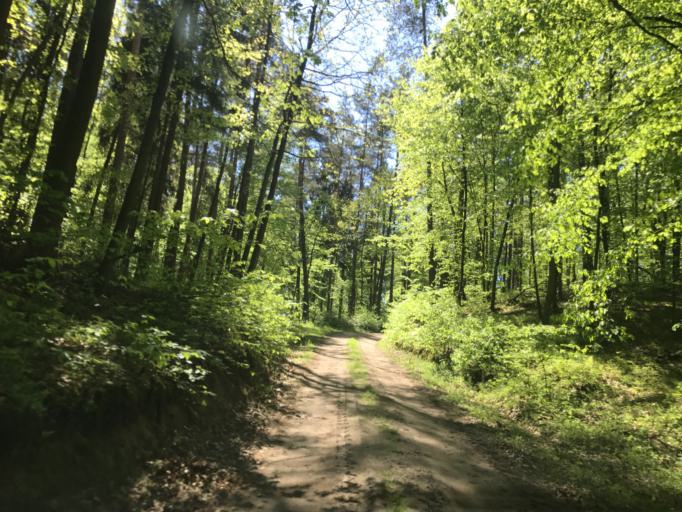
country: PL
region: Kujawsko-Pomorskie
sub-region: Powiat brodnicki
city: Gorzno
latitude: 53.2194
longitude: 19.7355
